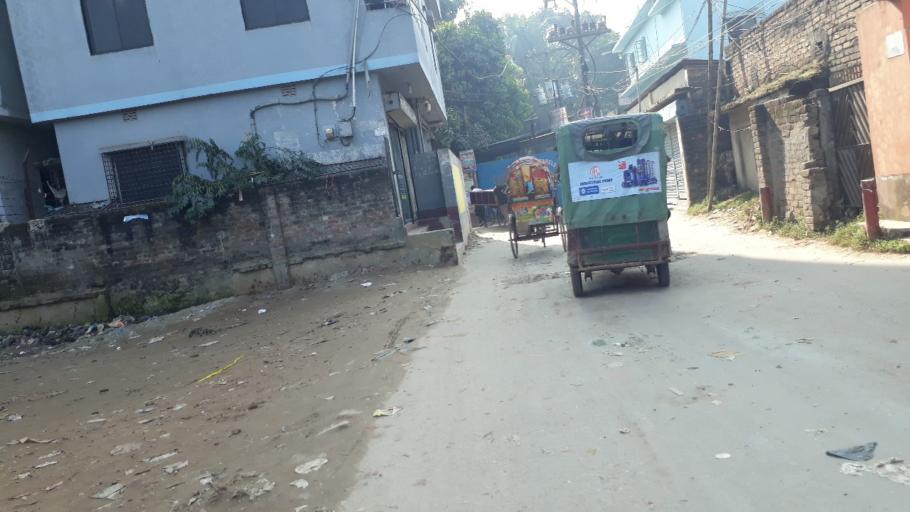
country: BD
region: Dhaka
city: Tungi
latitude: 23.8518
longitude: 90.2514
